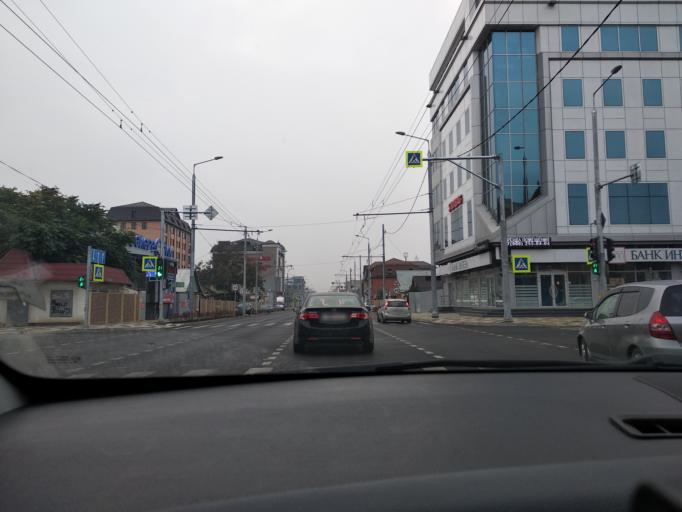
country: RU
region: Krasnodarskiy
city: Krasnodar
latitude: 45.0495
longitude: 38.9585
